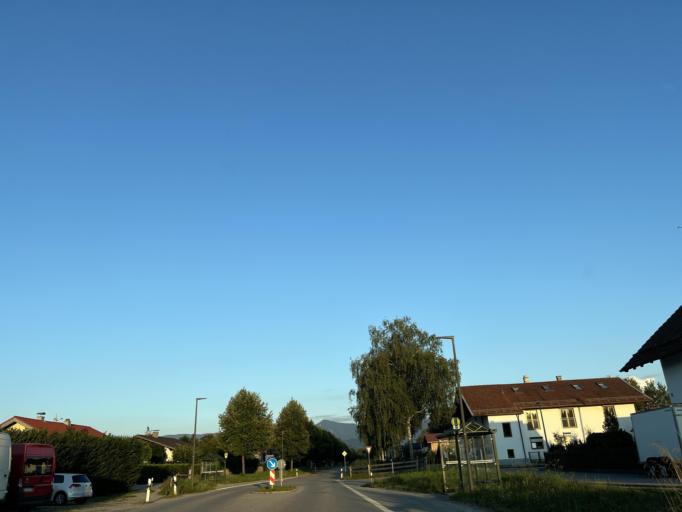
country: DE
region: Bavaria
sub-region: Upper Bavaria
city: Raubling
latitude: 47.7917
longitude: 12.0737
